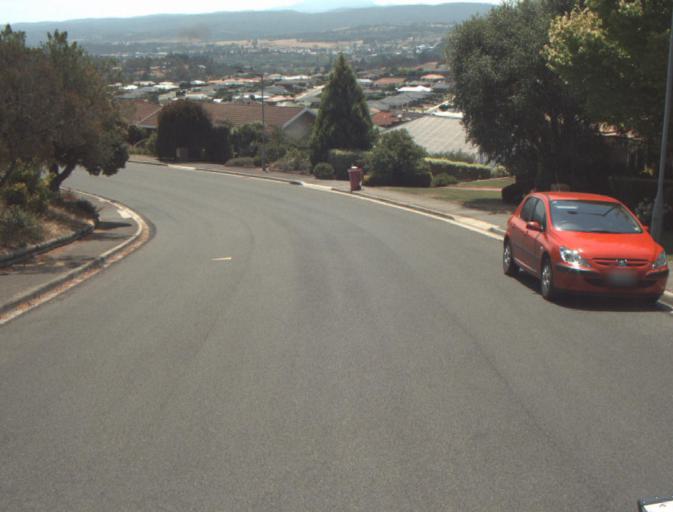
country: AU
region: Tasmania
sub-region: Launceston
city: Newstead
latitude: -41.4864
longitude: 147.1793
